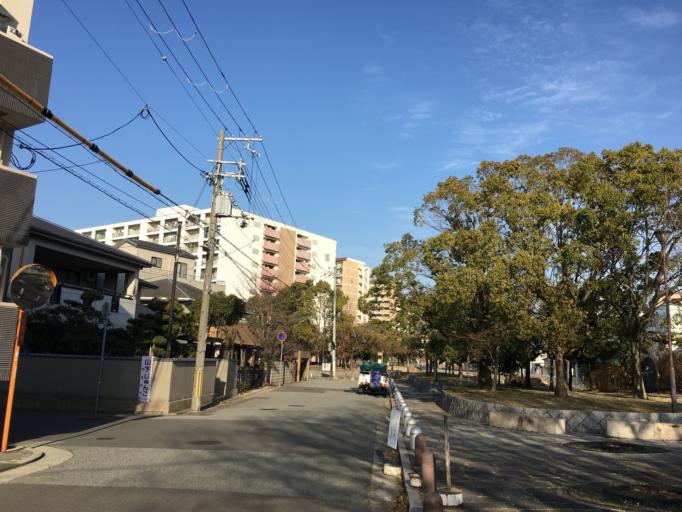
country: JP
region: Hyogo
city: Nishinomiya-hama
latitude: 34.7398
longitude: 135.3456
